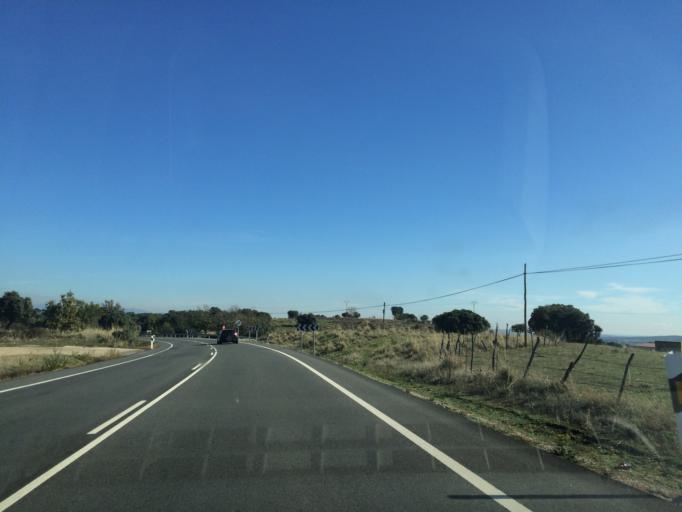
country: ES
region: Madrid
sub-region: Provincia de Madrid
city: Guadalix de la Sierra
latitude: 40.7707
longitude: -3.7306
